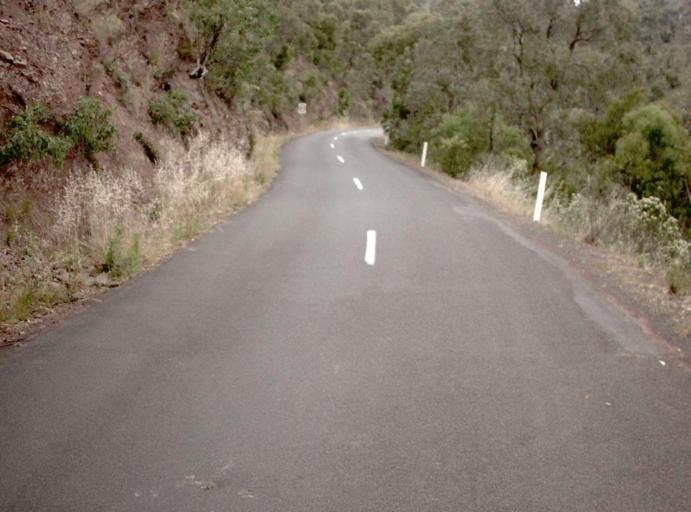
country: AU
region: Victoria
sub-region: Wellington
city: Heyfield
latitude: -37.7063
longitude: 146.6665
